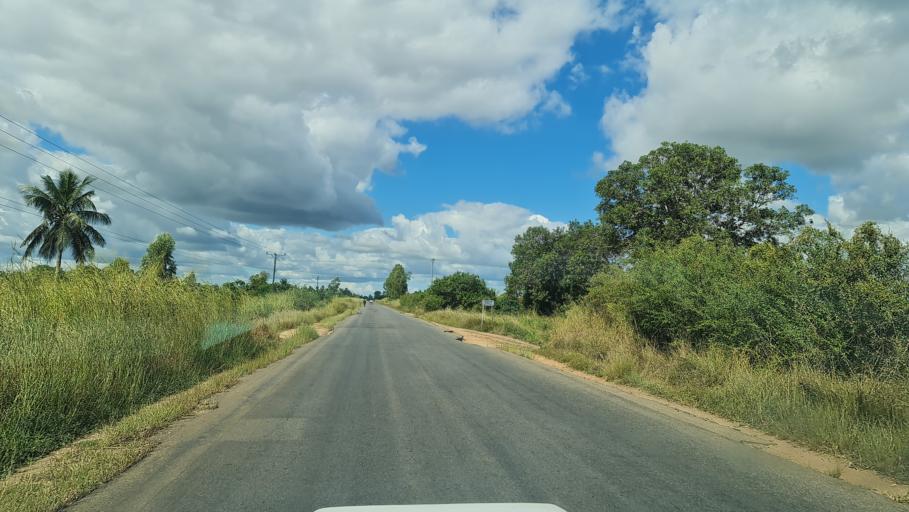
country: MZ
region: Zambezia
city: Quelimane
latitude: -17.5898
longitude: 36.7620
